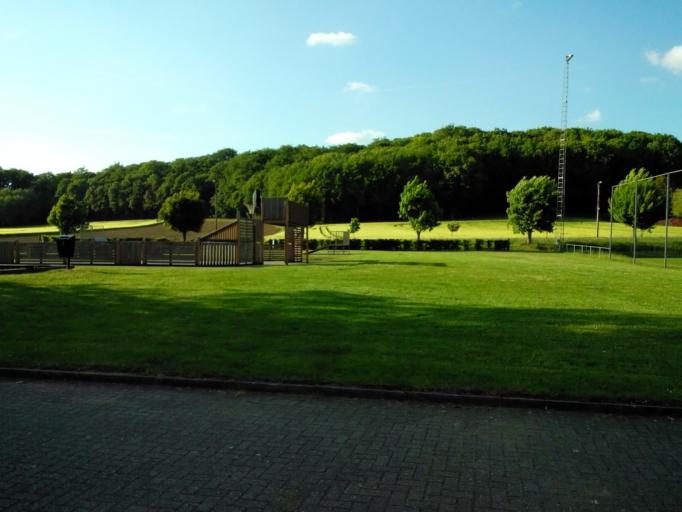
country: BE
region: Flanders
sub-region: Provincie Vlaams-Brabant
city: Holsbeek
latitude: 50.8957
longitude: 4.7647
